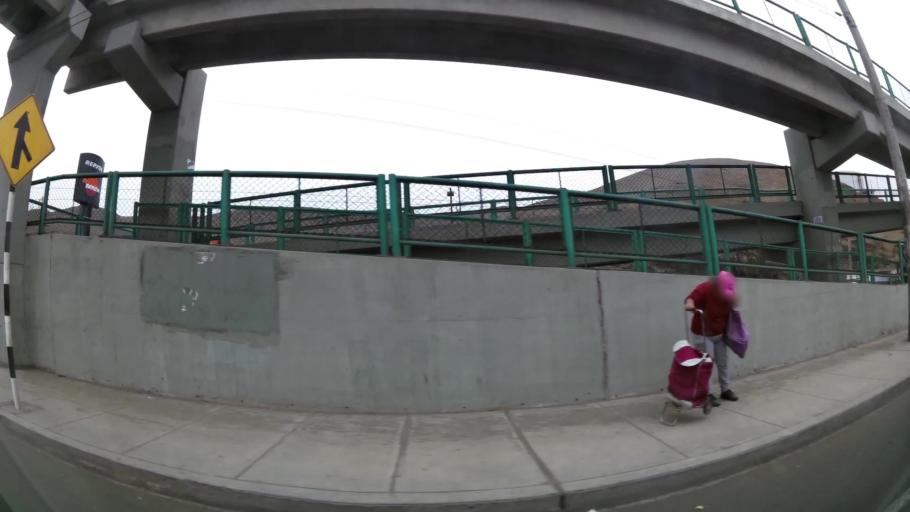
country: PE
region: Lima
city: Ventanilla
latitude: -11.9416
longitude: -77.1312
